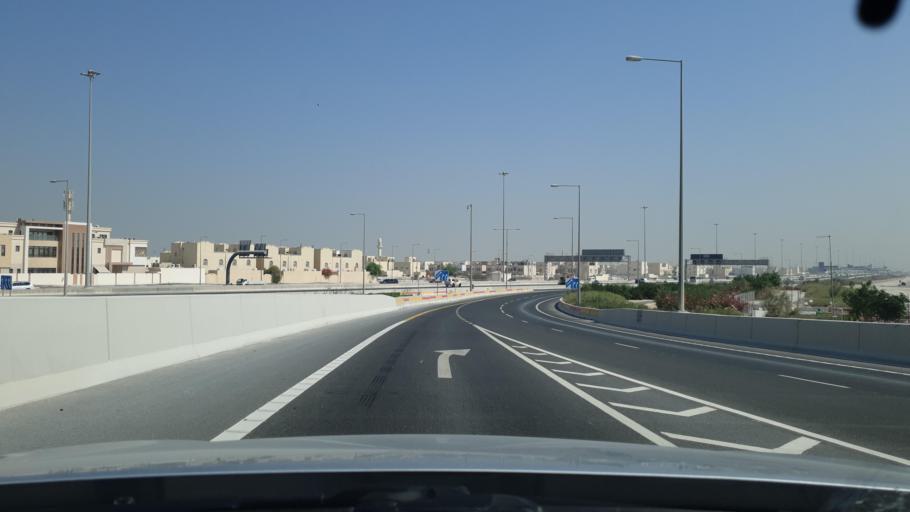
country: QA
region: Baladiyat ad Dawhah
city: Doha
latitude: 25.2207
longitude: 51.5373
